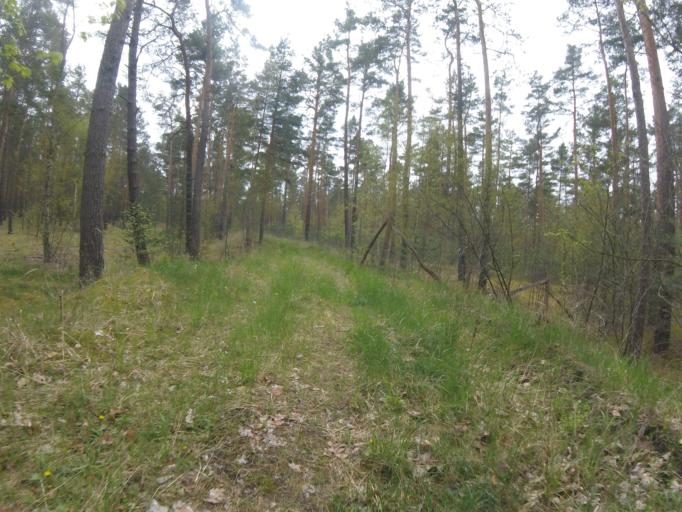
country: DE
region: Brandenburg
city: Bestensee
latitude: 52.2460
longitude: 13.6746
